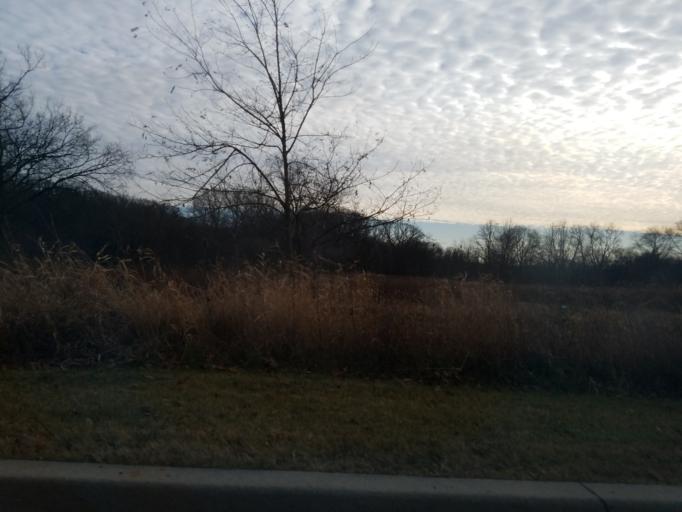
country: US
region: Illinois
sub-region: Will County
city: Mokena
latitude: 41.5269
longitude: -87.8710
